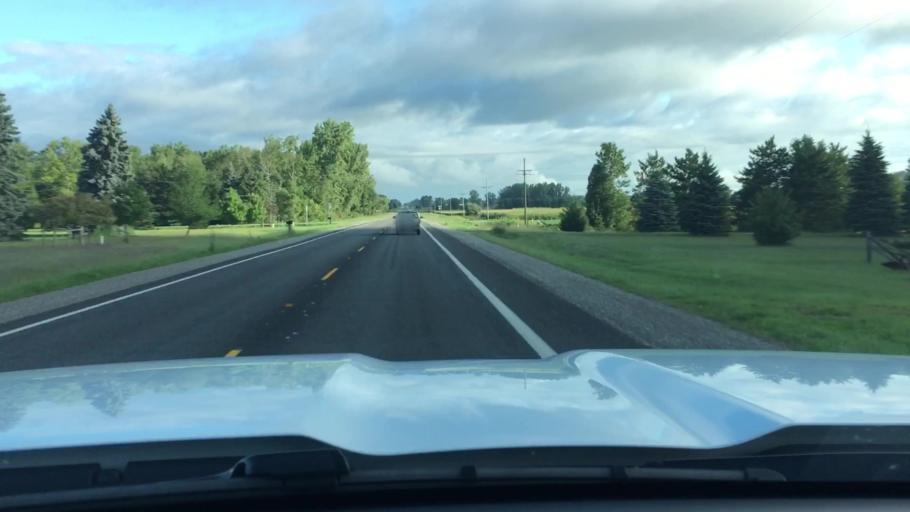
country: US
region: Michigan
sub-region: Tuscola County
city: Caro
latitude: 43.3701
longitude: -83.3831
